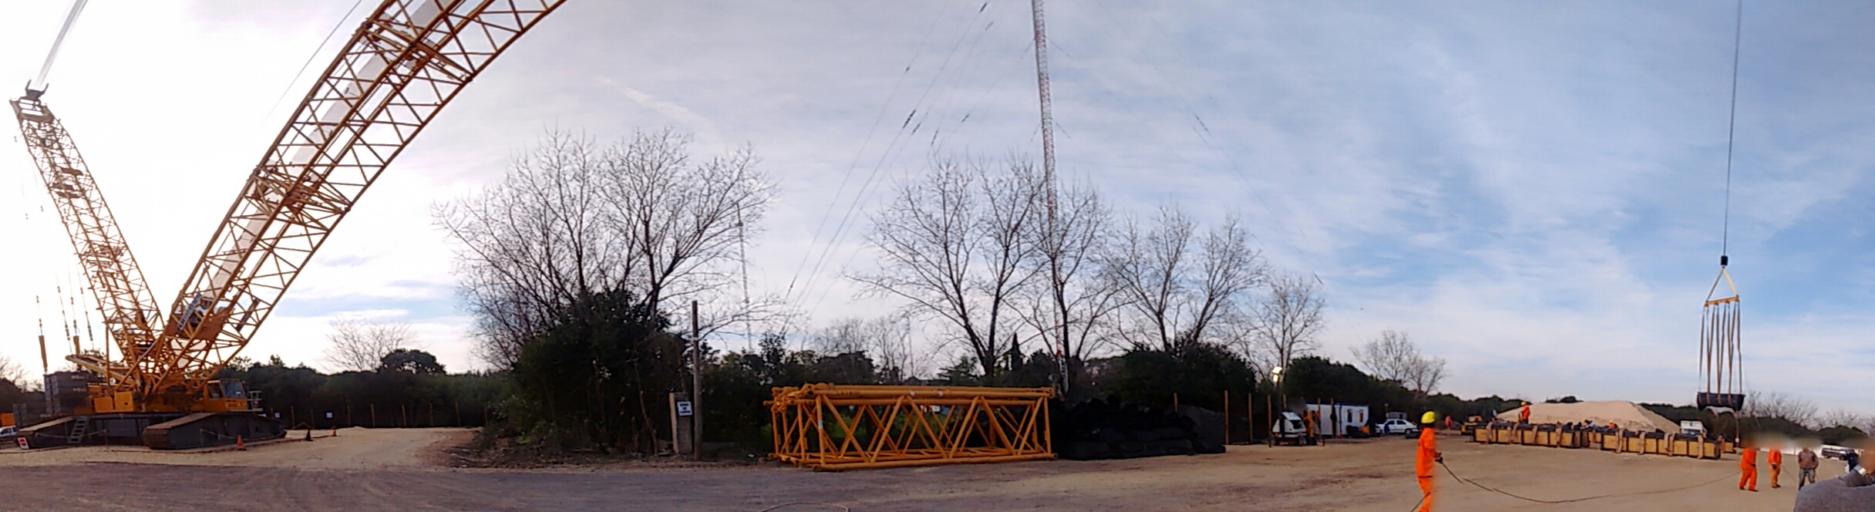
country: AR
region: Santa Fe
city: Gobernador Galvez
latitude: -33.0125
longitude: -60.6336
